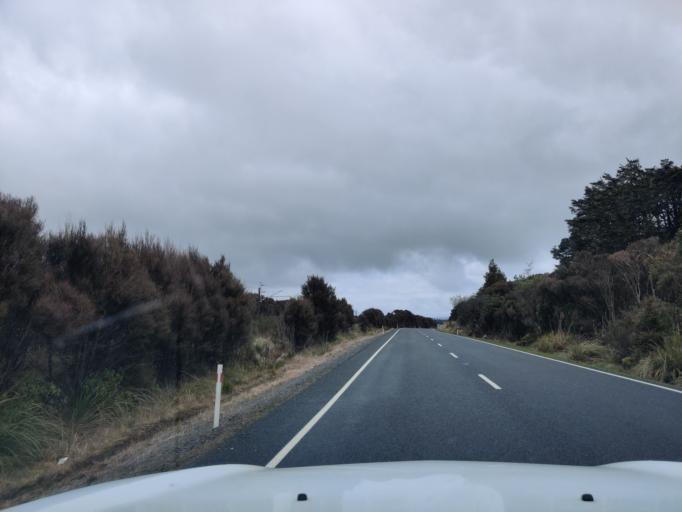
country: NZ
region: Manawatu-Wanganui
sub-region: Ruapehu District
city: Waiouru
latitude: -39.3318
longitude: 175.3813
